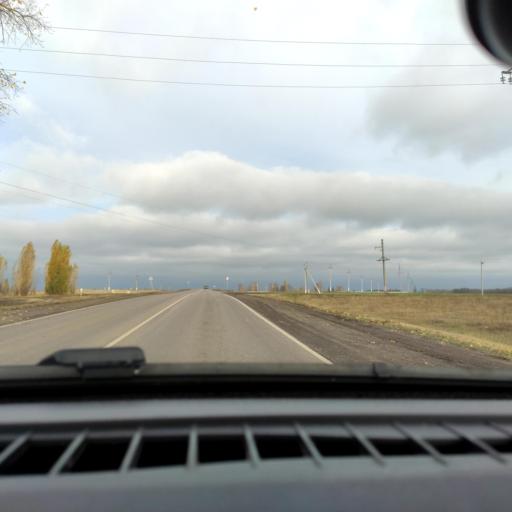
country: RU
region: Belgorod
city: Ilovka
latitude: 50.6966
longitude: 38.6584
